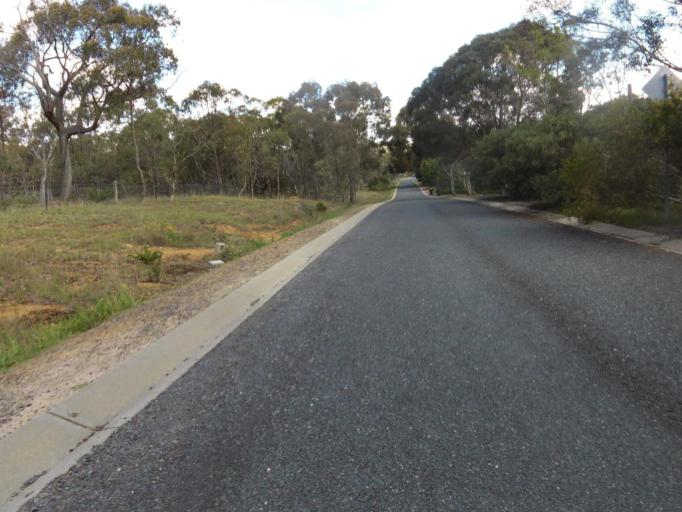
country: AU
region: Australian Capital Territory
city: Belconnen
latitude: -35.1664
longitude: 149.0708
